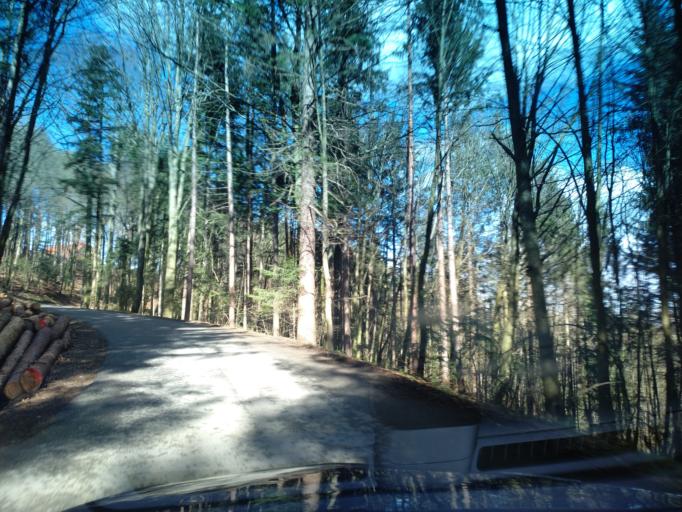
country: AT
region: Styria
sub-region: Politischer Bezirk Leibnitz
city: Sankt Johann im Saggautal
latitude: 46.7170
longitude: 15.3862
